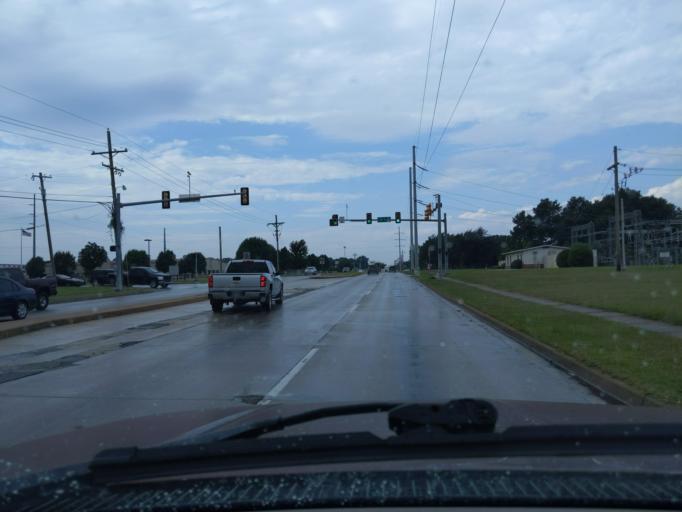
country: US
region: Oklahoma
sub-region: Tulsa County
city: Broken Arrow
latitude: 36.1336
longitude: -95.8749
